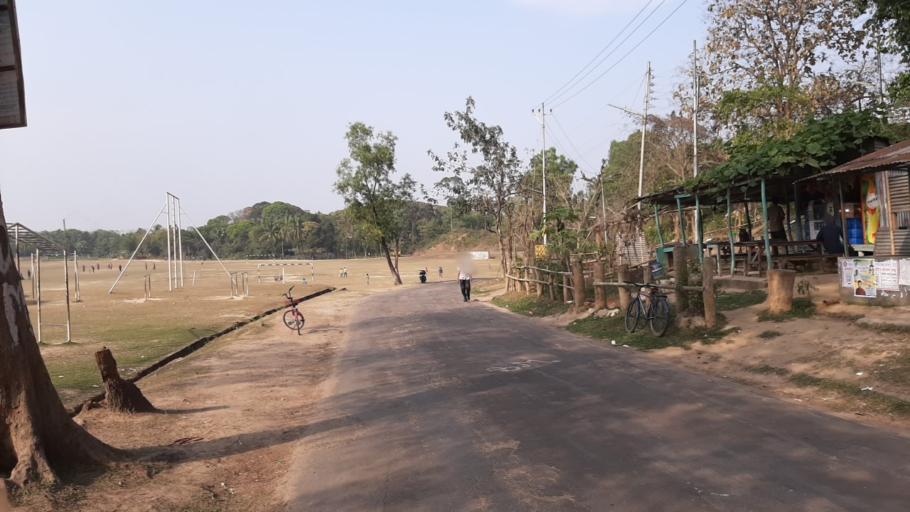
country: BD
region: Chittagong
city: Raojan
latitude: 22.4790
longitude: 91.7909
